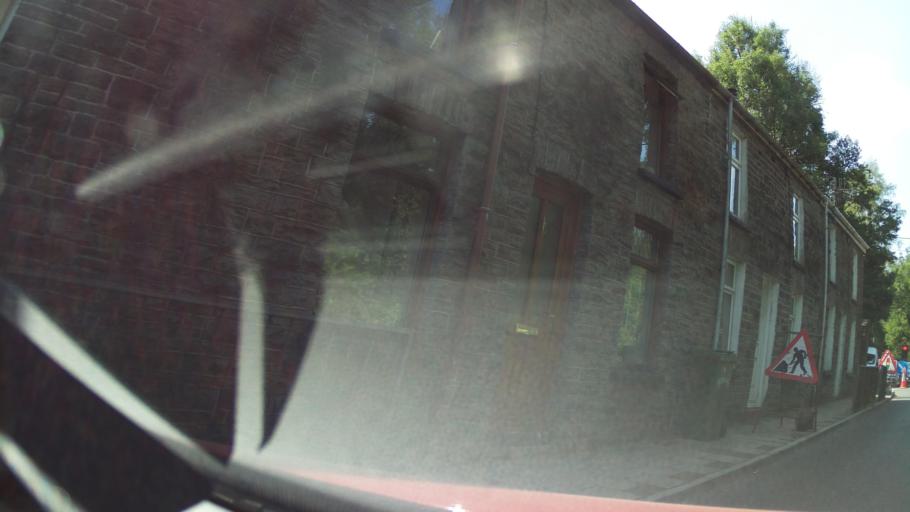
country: GB
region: Wales
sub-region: Caerphilly County Borough
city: Bargoed
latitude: 51.6964
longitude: -3.2356
